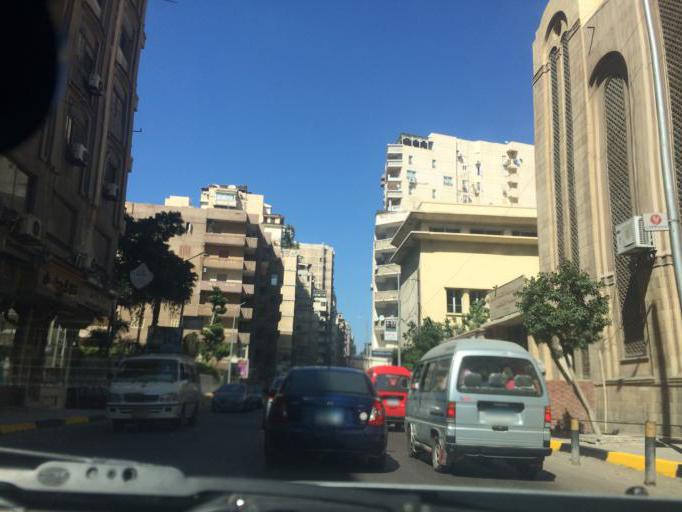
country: EG
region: Alexandria
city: Alexandria
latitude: 31.2447
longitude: 29.9721
